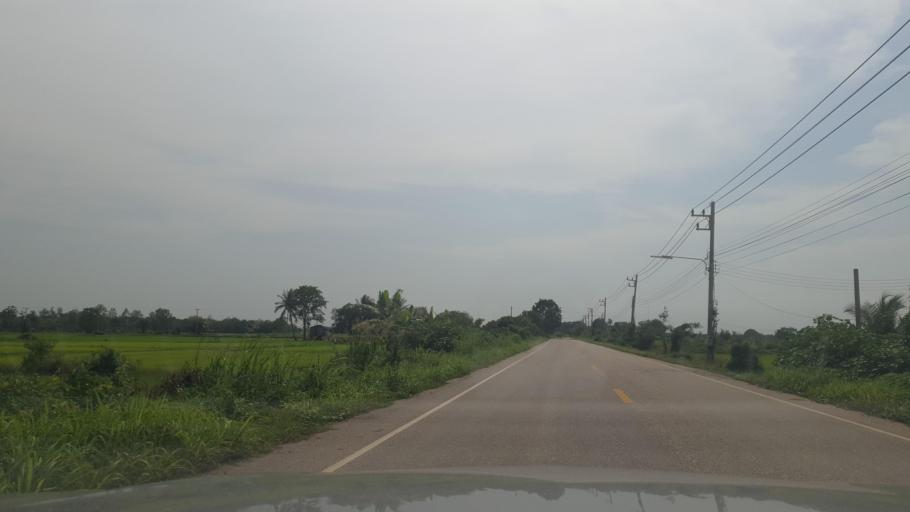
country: TH
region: Sukhothai
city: Si Samrong
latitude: 17.1158
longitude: 99.8844
